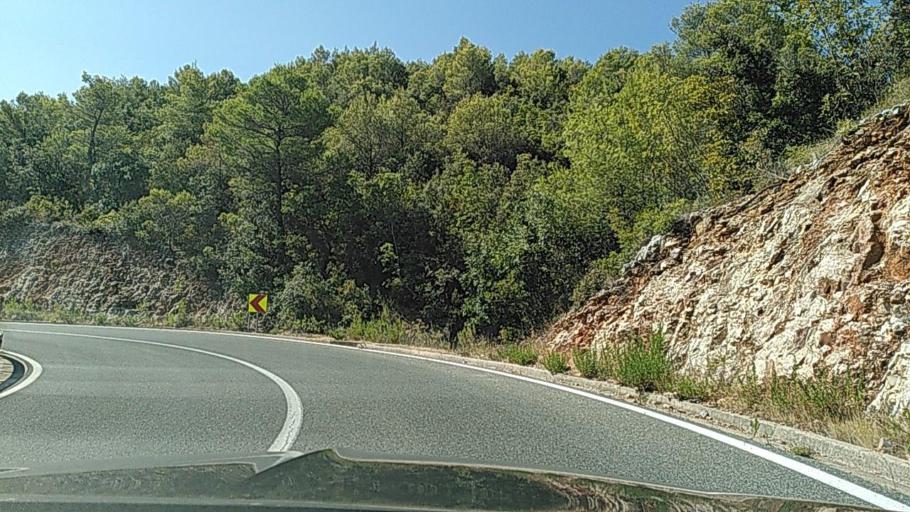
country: HR
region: Splitsko-Dalmatinska
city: Jelsa
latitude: 43.1440
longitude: 16.7742
